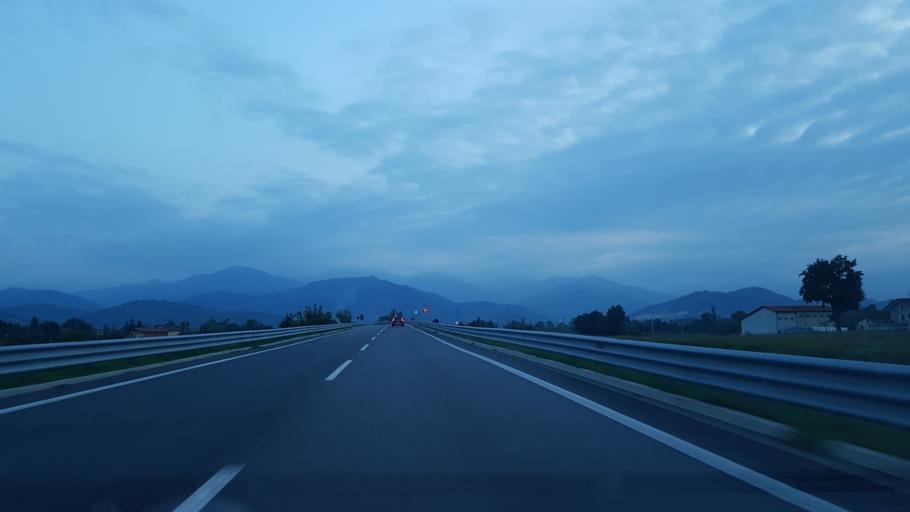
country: IT
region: Piedmont
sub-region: Provincia di Cuneo
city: Mondovi
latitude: 44.3789
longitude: 7.7912
